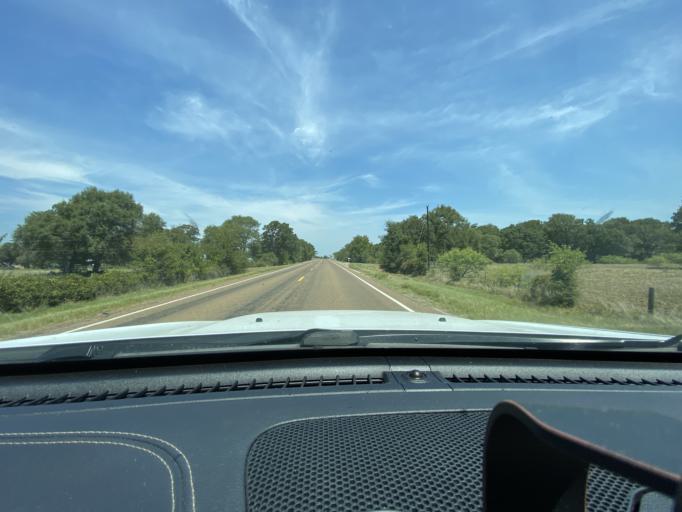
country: US
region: Texas
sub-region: Bastrop County
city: Smithville
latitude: 30.1109
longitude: -97.0801
